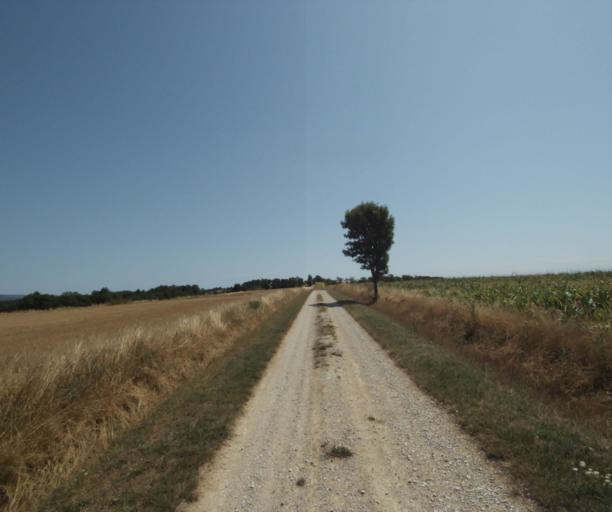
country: FR
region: Midi-Pyrenees
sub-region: Departement de la Haute-Garonne
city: Saint-Felix-Lauragais
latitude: 43.4531
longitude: 1.8553
